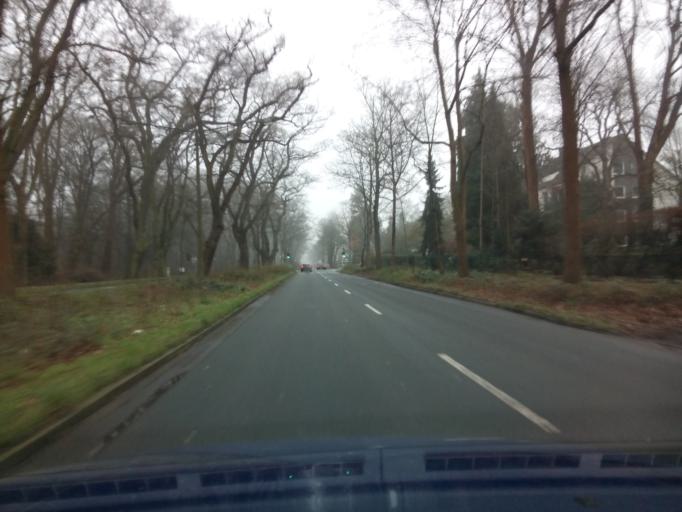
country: DE
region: Bremen
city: Bremen
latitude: 53.0960
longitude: 8.8346
